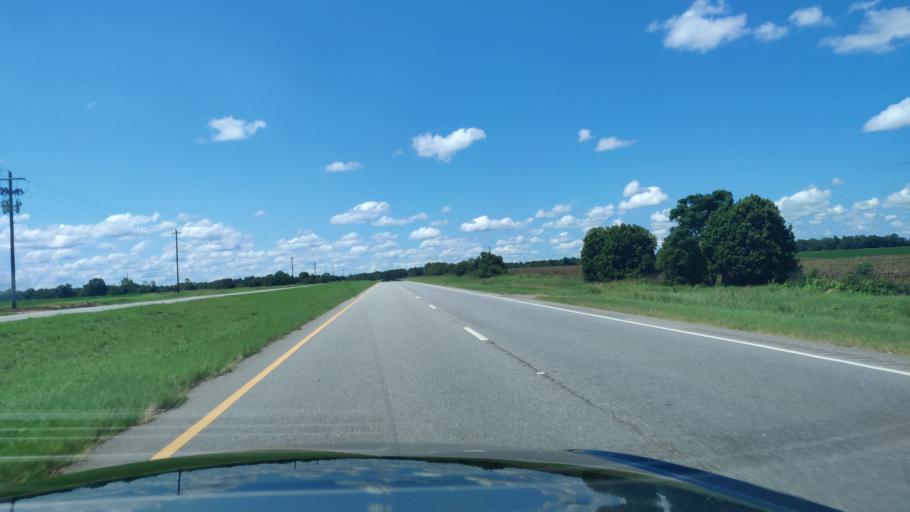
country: US
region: Georgia
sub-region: Terrell County
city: Dawson
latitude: 31.8432
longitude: -84.4708
